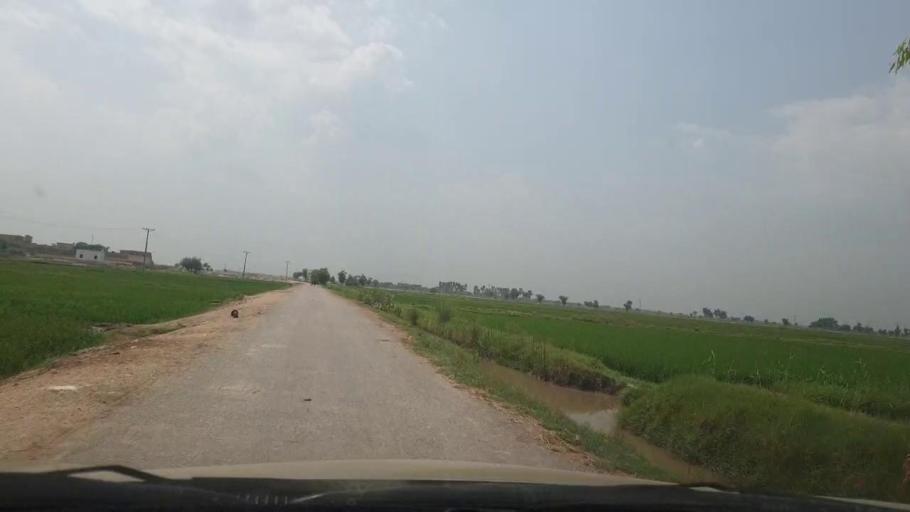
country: PK
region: Sindh
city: Ratodero
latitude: 27.7005
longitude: 68.2566
